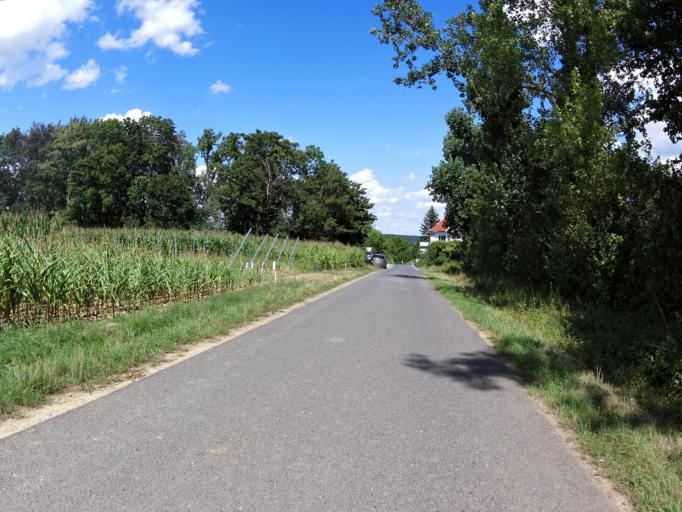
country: DE
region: Bavaria
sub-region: Regierungsbezirk Unterfranken
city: Prosselsheim
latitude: 49.8679
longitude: 10.1572
